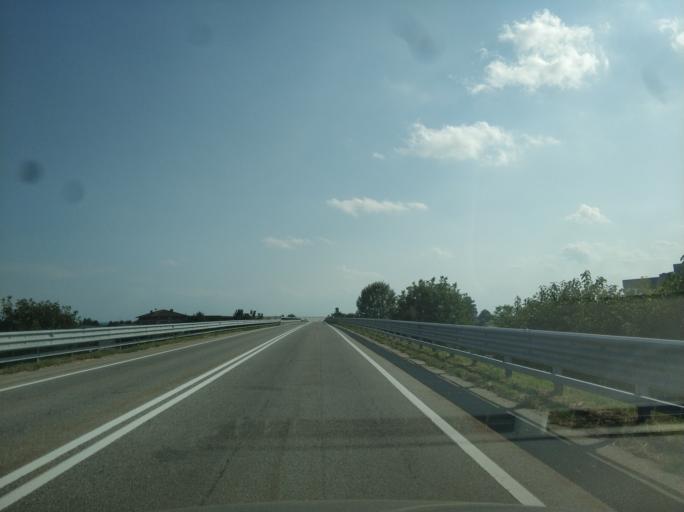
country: IT
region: Piedmont
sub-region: Provincia di Cuneo
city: Roreto
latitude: 44.6692
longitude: 7.8247
